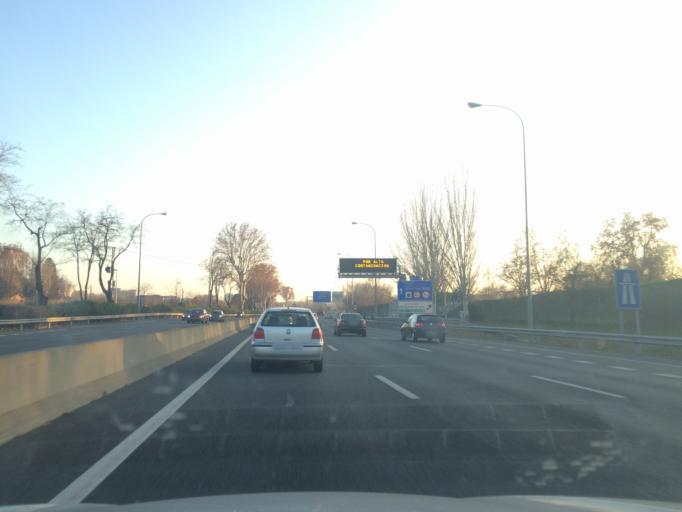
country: ES
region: Madrid
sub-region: Provincia de Madrid
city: Moncloa-Aravaca
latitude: 40.4434
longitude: -3.7394
